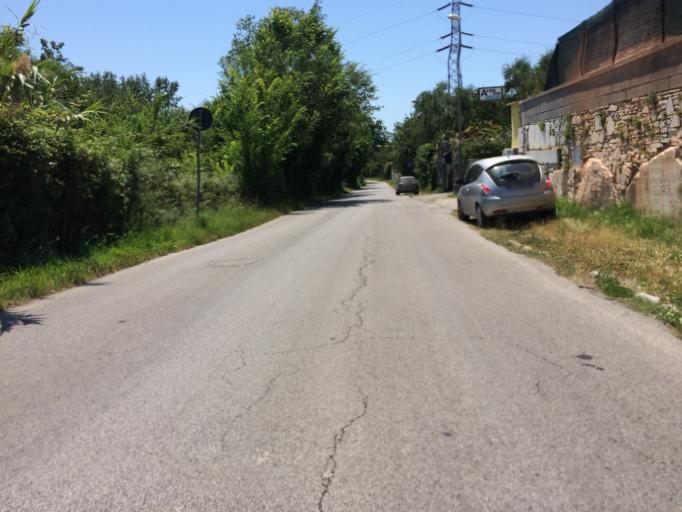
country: IT
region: Tuscany
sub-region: Provincia di Massa-Carrara
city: Massa
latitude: 44.0357
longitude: 10.1246
